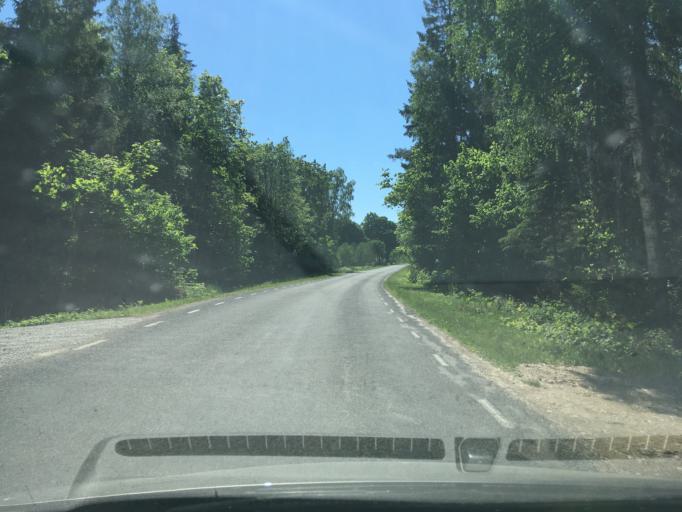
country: EE
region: Raplamaa
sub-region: Kohila vald
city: Kohila
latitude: 59.1564
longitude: 24.8524
